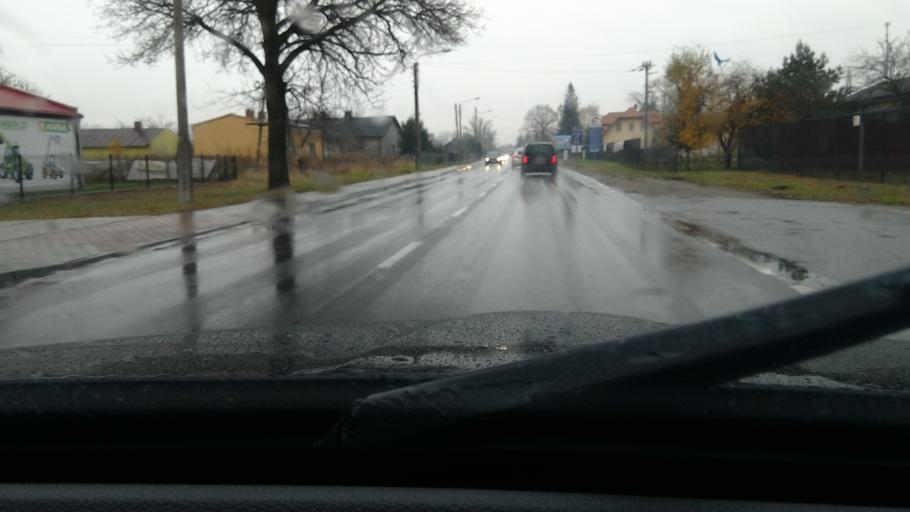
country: PL
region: Lodz Voivodeship
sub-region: Skierniewice
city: Skierniewice
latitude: 51.9772
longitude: 20.1294
